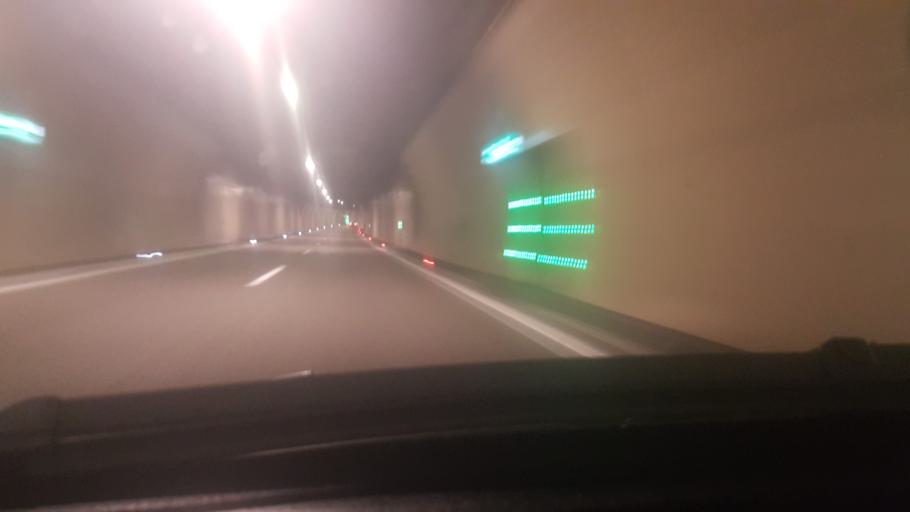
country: AT
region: Carinthia
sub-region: Klagenfurt am Woerthersee
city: Klagenfurt am Woerthersee
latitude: 46.6538
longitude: 14.3087
